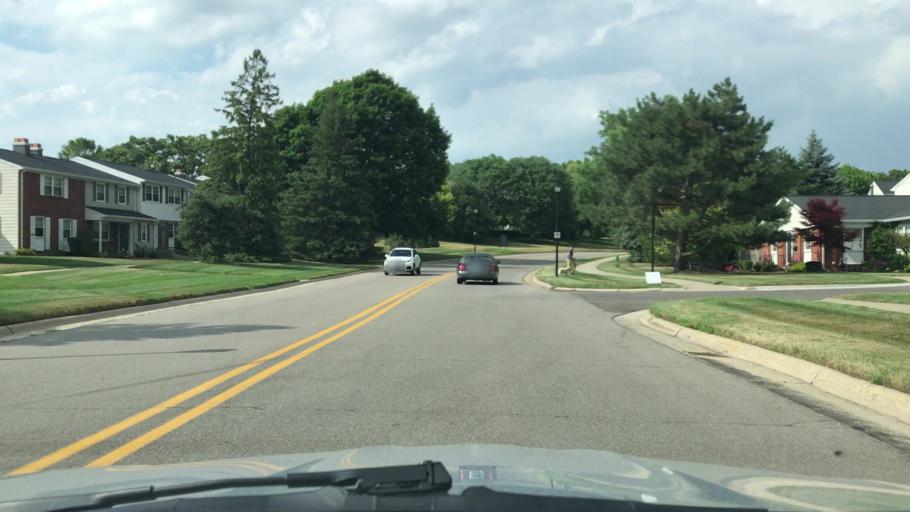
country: US
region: Michigan
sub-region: Wayne County
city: Northville
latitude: 42.4340
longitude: -83.4648
